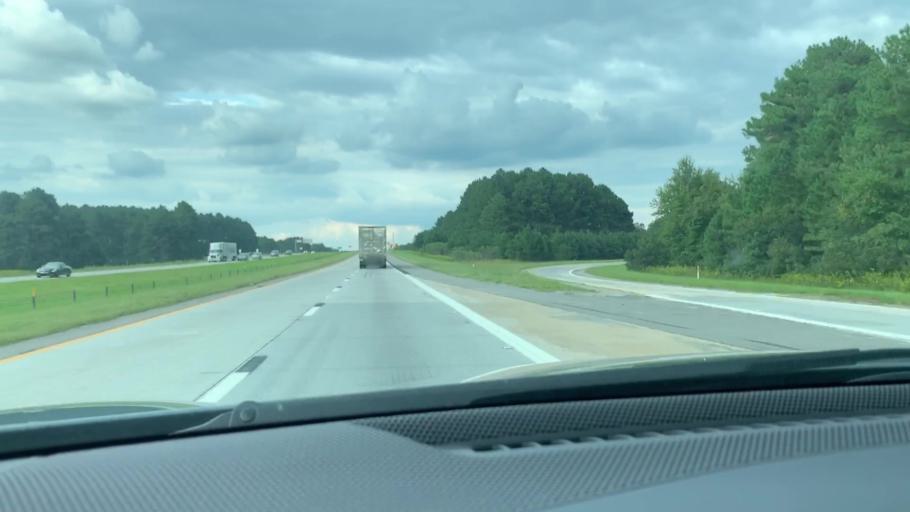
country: US
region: South Carolina
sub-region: Dorchester County
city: Saint George
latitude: 33.3144
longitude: -80.5507
